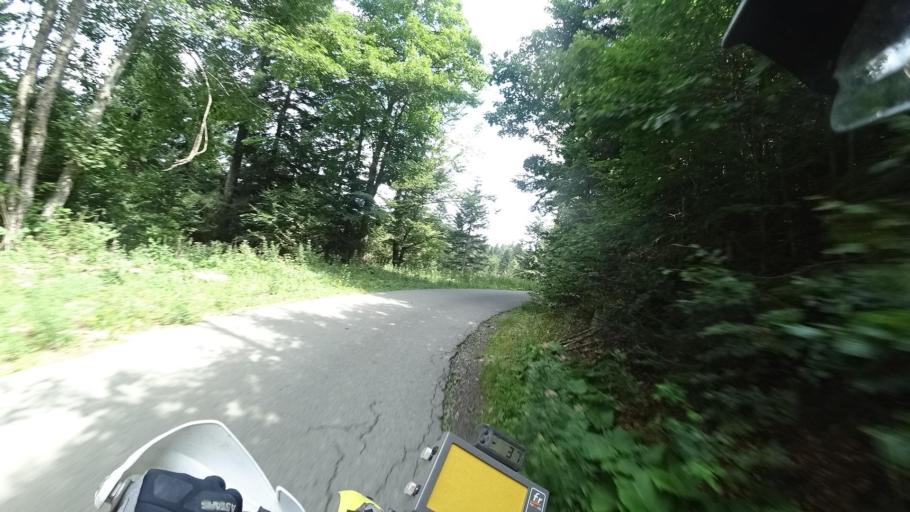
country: HR
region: Licko-Senjska
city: Senj
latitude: 45.1064
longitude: 15.0078
